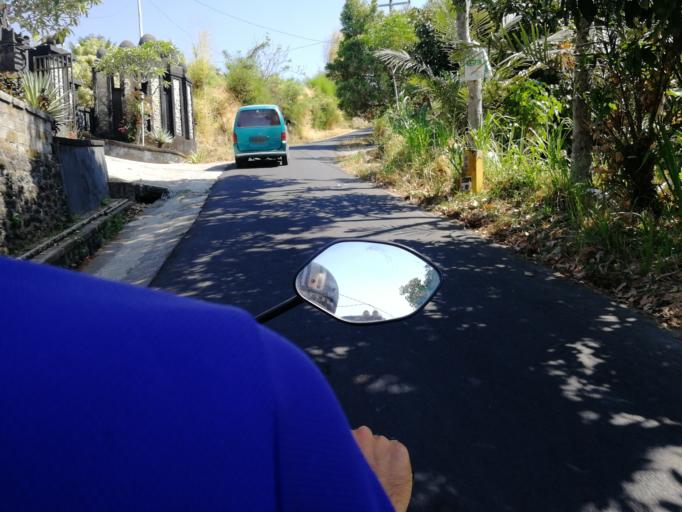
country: ID
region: Bali
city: Banjar Kedisan
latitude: -8.1602
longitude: 115.3055
